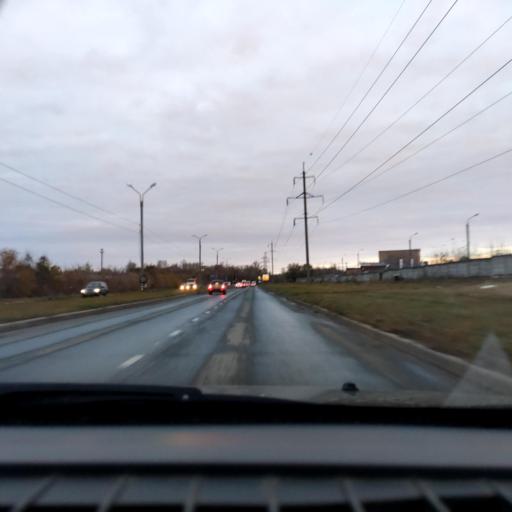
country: RU
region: Samara
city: Tol'yatti
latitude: 53.5553
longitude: 49.3192
